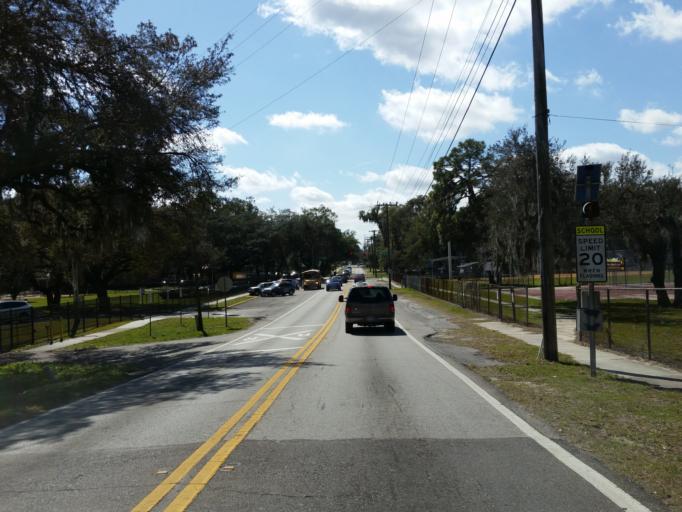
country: US
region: Florida
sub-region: Hillsborough County
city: Brandon
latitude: 27.9431
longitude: -82.2776
